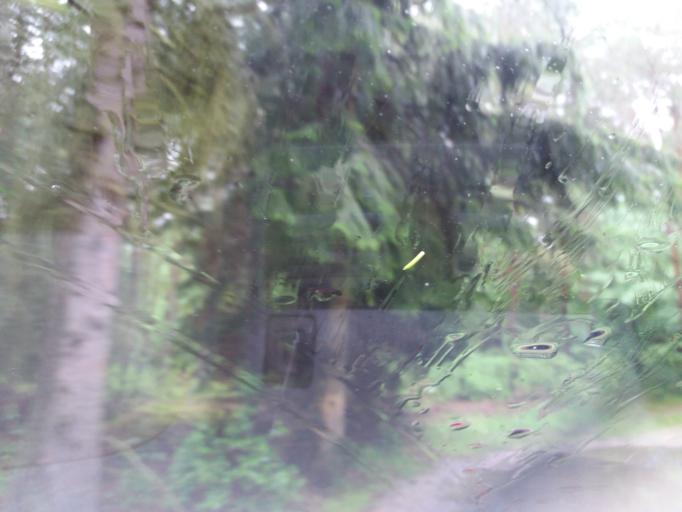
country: PL
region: Lubusz
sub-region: Powiat strzelecko-drezdenecki
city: Dobiegniew
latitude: 53.0139
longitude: 15.8521
